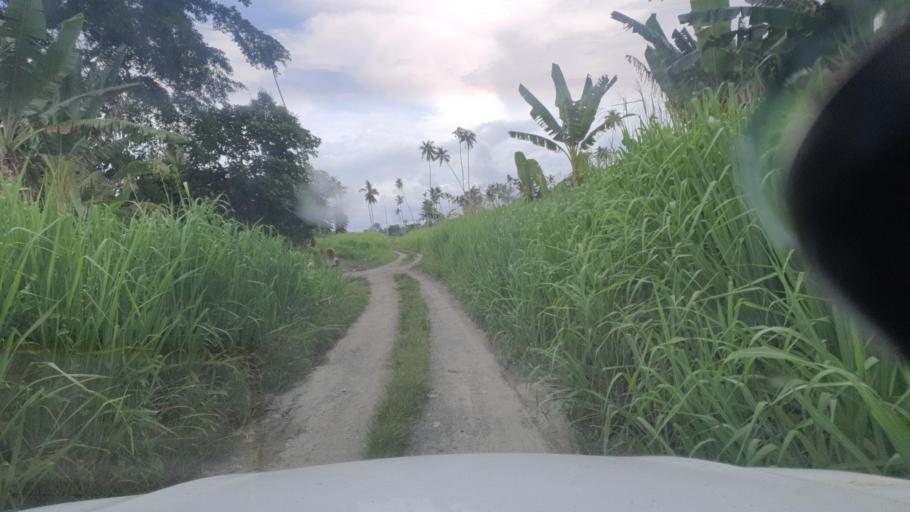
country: SB
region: Guadalcanal
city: Honiara
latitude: -9.4378
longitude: 160.2825
